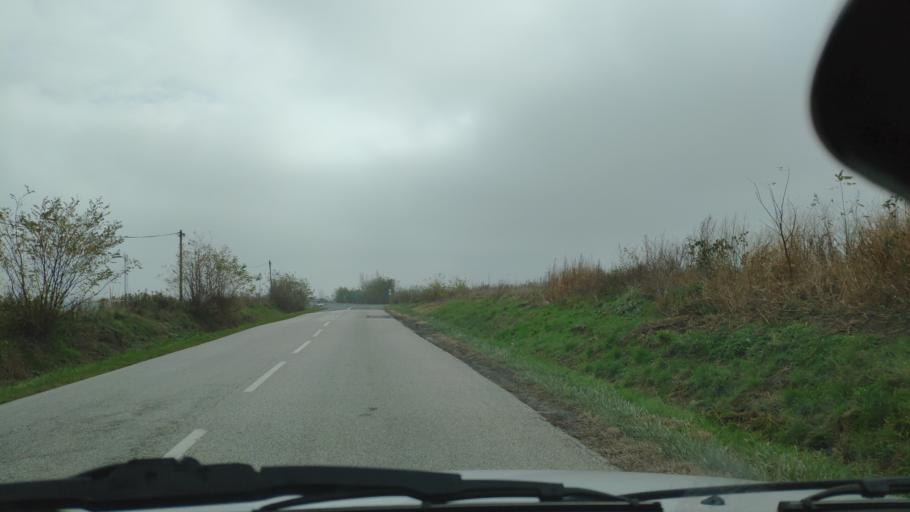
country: HU
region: Somogy
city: Balatonbereny
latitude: 46.6532
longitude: 17.2975
